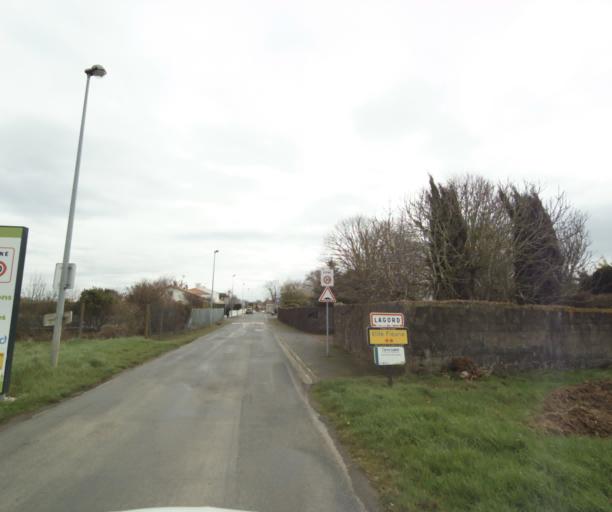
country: FR
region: Poitou-Charentes
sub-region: Departement de la Charente-Maritime
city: Lagord
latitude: 46.1922
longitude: -1.1600
